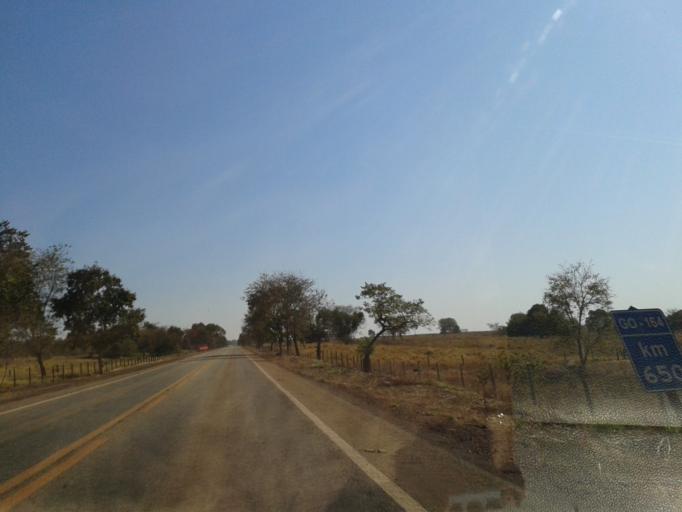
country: BR
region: Goias
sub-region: Mozarlandia
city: Mozarlandia
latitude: -14.7243
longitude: -50.5461
